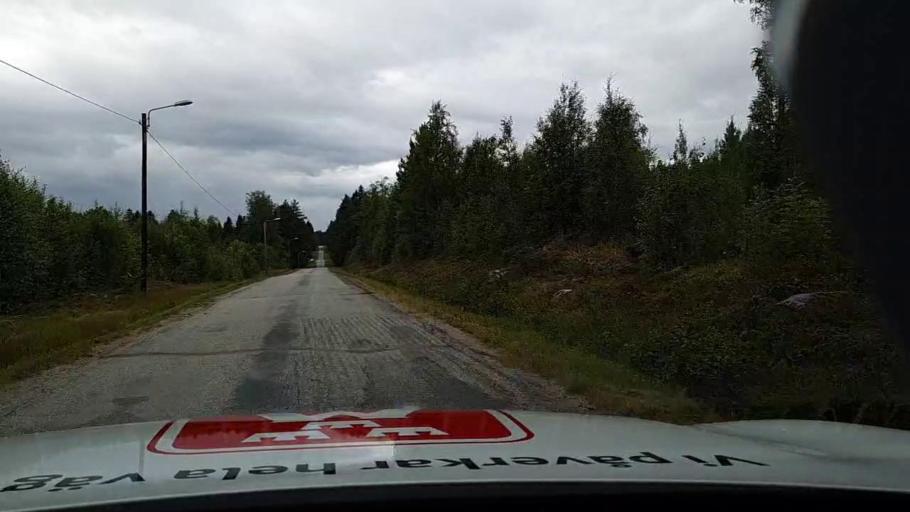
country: SE
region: Vaesterbotten
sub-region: Dorotea Kommun
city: Dorotea
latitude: 64.0984
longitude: 16.4134
